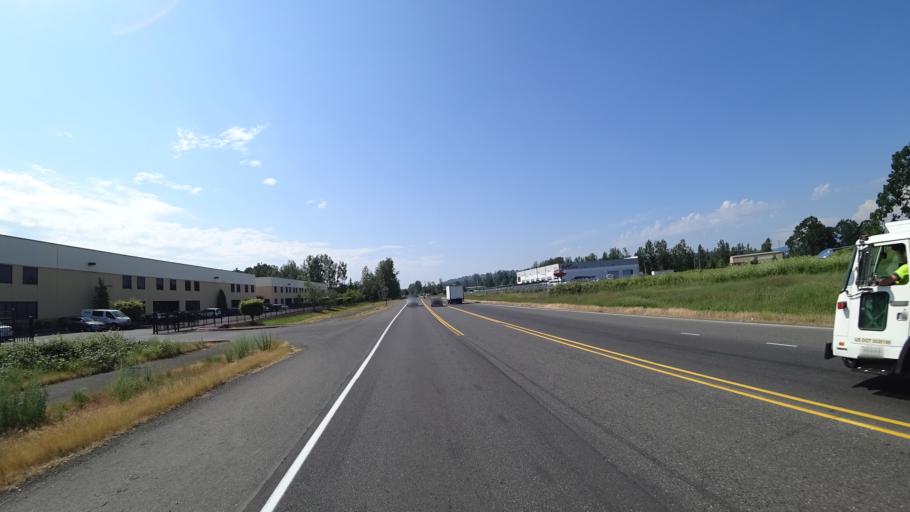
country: US
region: Oregon
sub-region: Multnomah County
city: Wood Village
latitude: 45.5499
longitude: -122.4190
